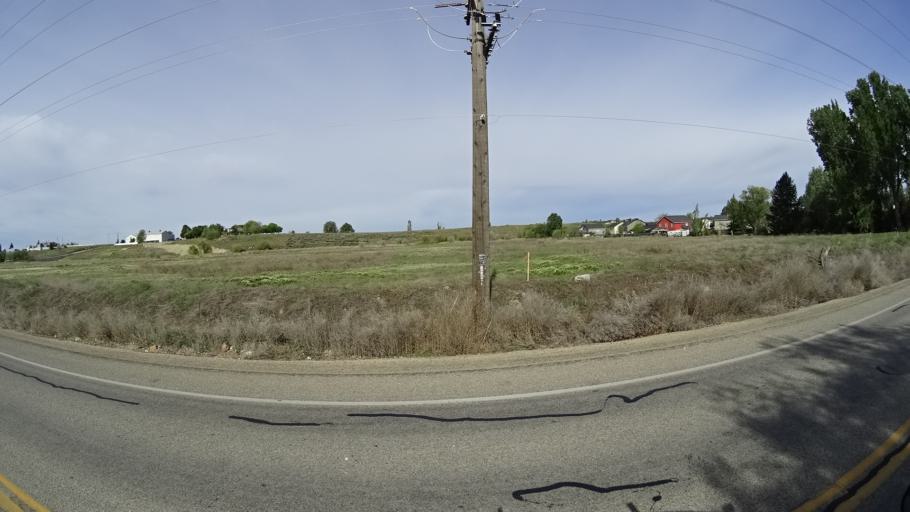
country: US
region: Idaho
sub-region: Ada County
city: Kuna
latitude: 43.5349
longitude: -116.3342
